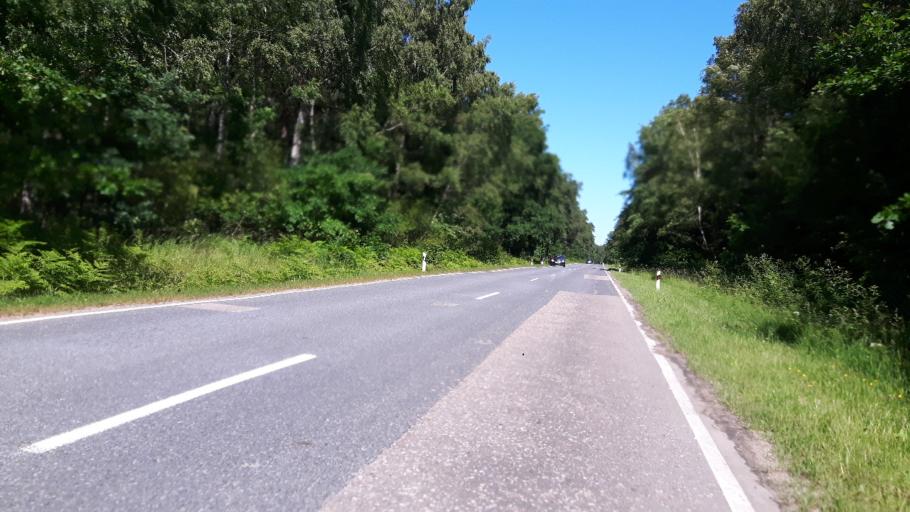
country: RU
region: Kaliningrad
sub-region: Zelenogradskiy Rayon
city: Zelenogradsk
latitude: 54.9845
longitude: 20.5476
